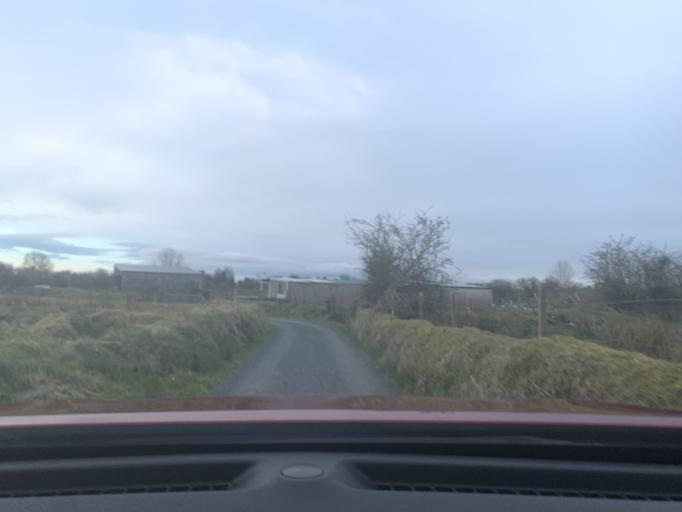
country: IE
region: Connaught
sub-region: Roscommon
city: Ballaghaderreen
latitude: 53.8971
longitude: -8.5901
